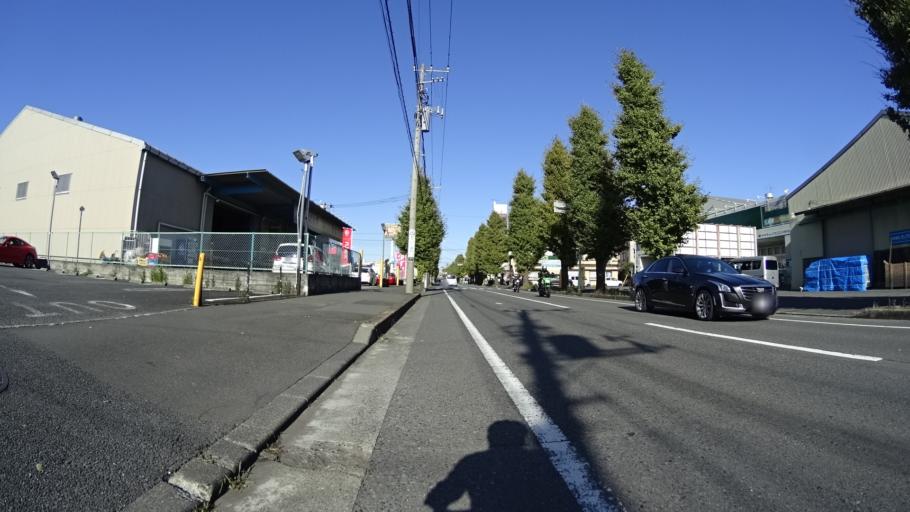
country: JP
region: Kanagawa
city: Zama
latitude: 35.5715
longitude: 139.3589
